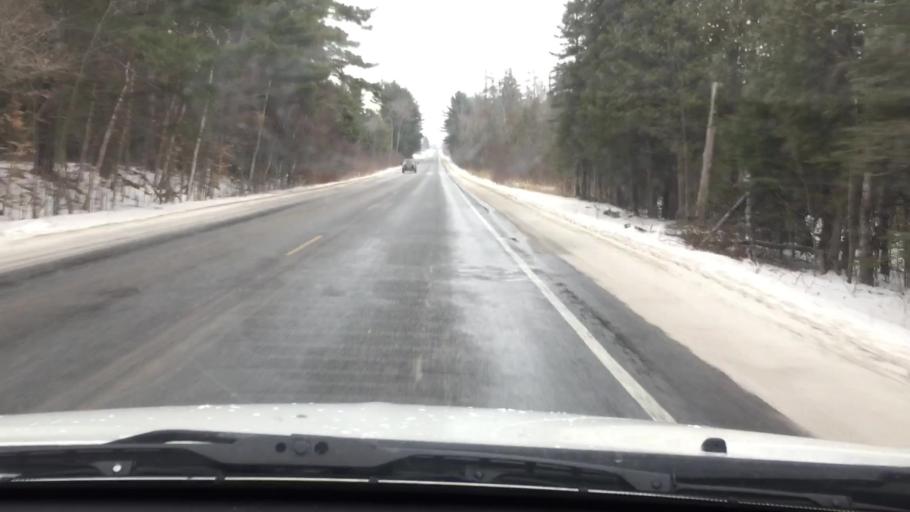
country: US
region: Michigan
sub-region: Osceola County
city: Reed City
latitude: 44.0568
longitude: -85.4440
